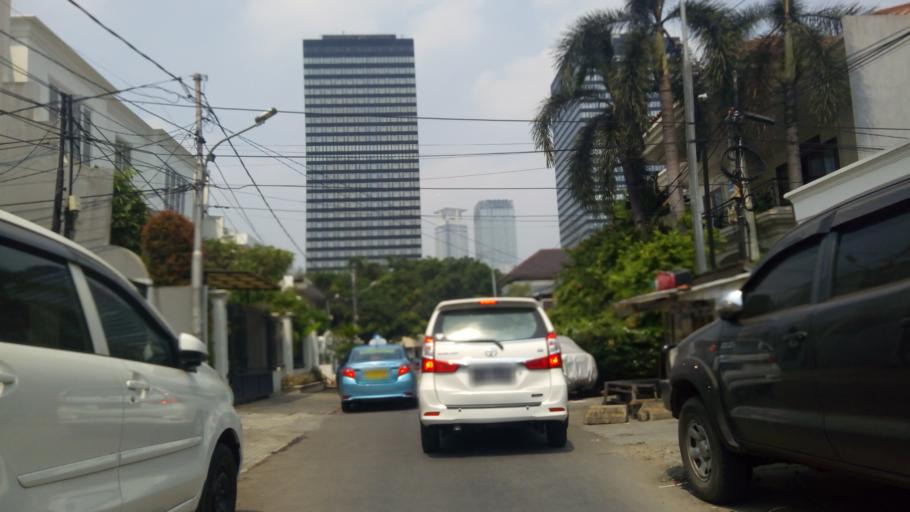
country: ID
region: Jakarta Raya
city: Jakarta
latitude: -6.2014
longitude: 106.8251
